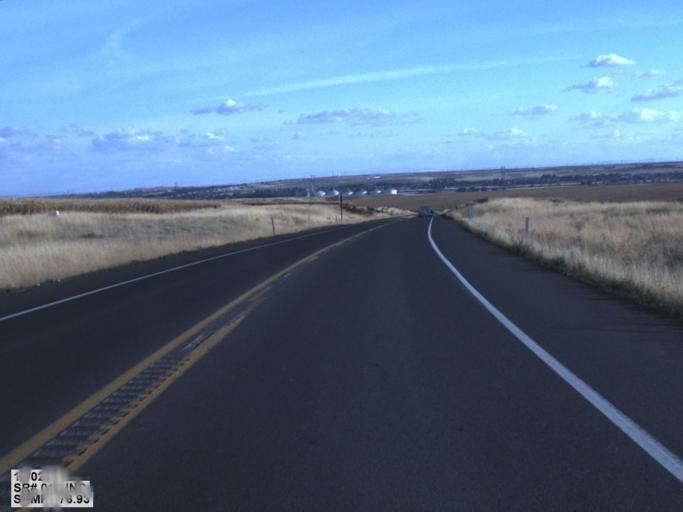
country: US
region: Oregon
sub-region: Umatilla County
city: Umatilla
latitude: 45.9570
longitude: -119.4076
